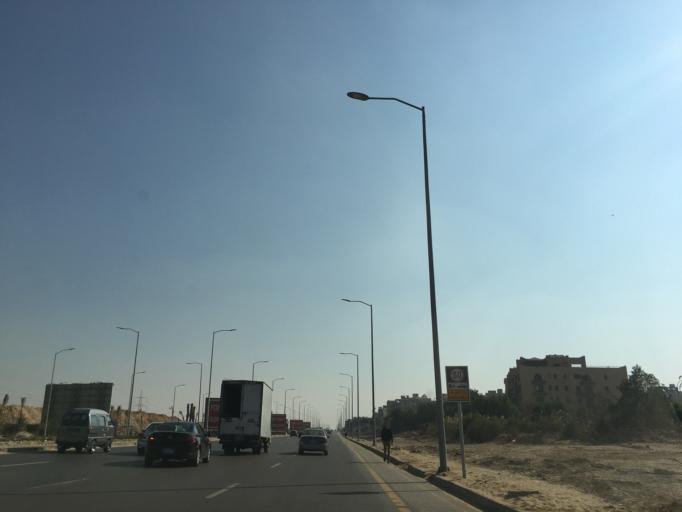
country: EG
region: Al Jizah
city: Awsim
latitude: 30.0028
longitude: 30.9867
